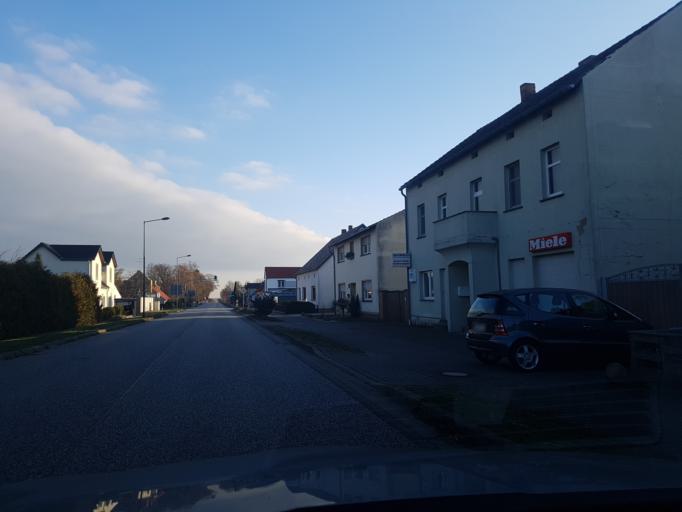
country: DE
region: Brandenburg
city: Luckau
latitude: 51.8326
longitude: 13.6411
